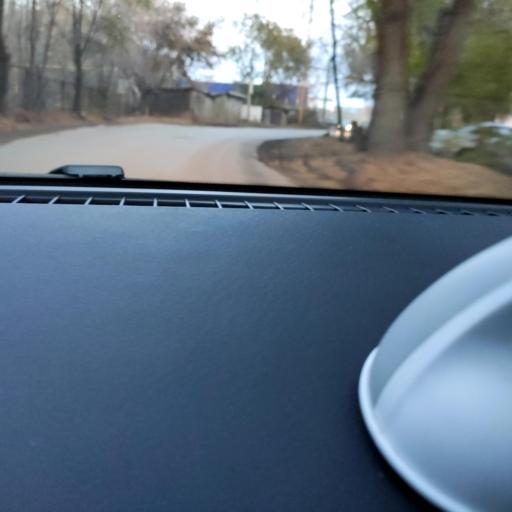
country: RU
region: Samara
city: Samara
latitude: 53.2025
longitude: 50.2496
